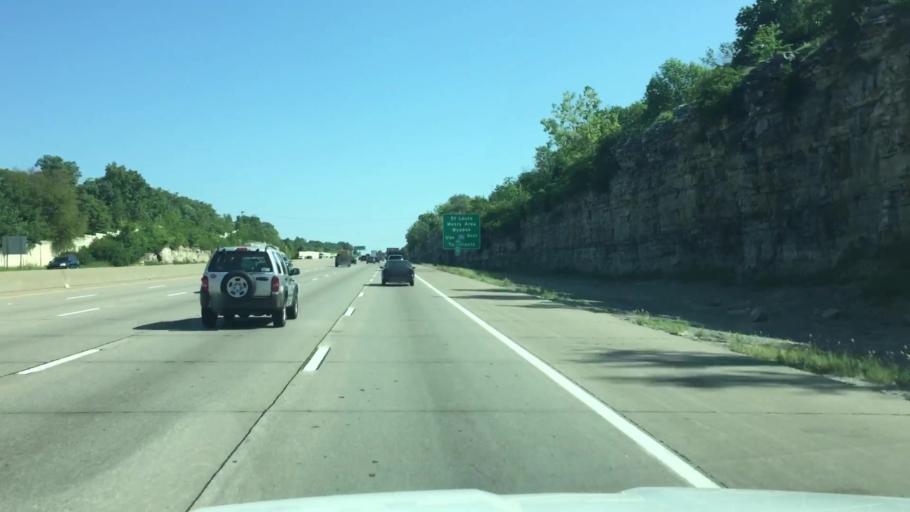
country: US
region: Missouri
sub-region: Jefferson County
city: Arnold
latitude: 38.4697
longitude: -90.3684
